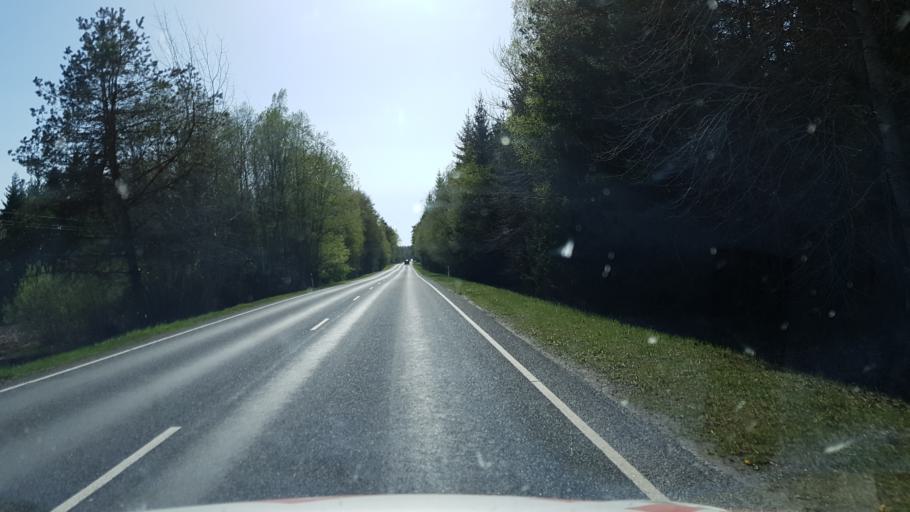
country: EE
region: Viljandimaa
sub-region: Abja vald
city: Abja-Paluoja
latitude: 58.2653
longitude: 25.2531
